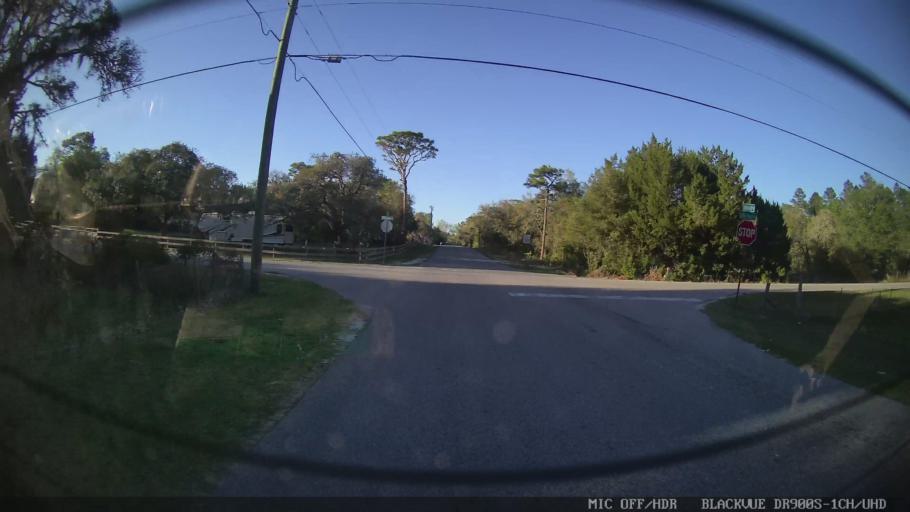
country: US
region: Florida
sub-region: Pasco County
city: Shady Hills
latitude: 28.3993
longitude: -82.5737
